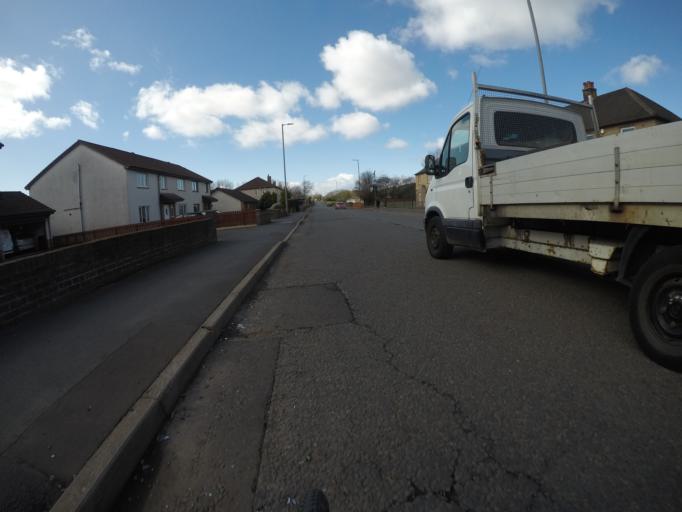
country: GB
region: Scotland
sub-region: North Ayrshire
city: Springside
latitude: 55.6134
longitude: -4.5971
